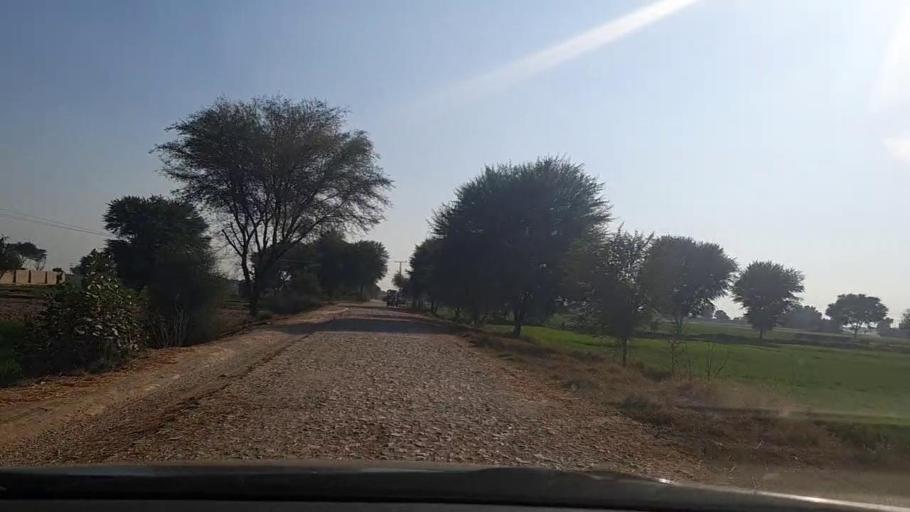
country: PK
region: Sindh
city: Sehwan
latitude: 26.3187
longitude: 68.0062
